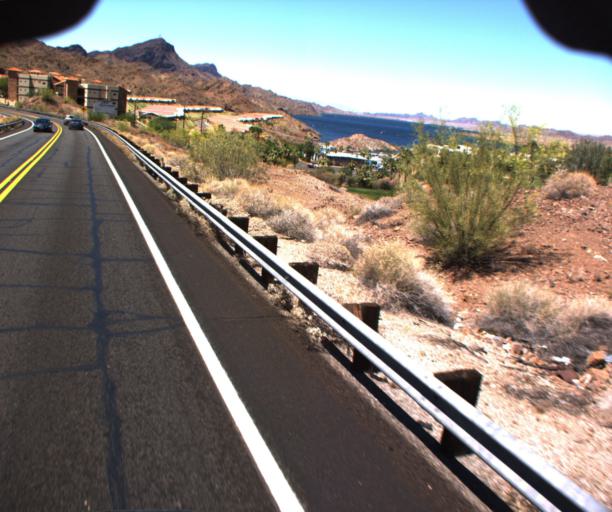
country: US
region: Arizona
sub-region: La Paz County
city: Cienega Springs
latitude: 34.2933
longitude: -114.1249
